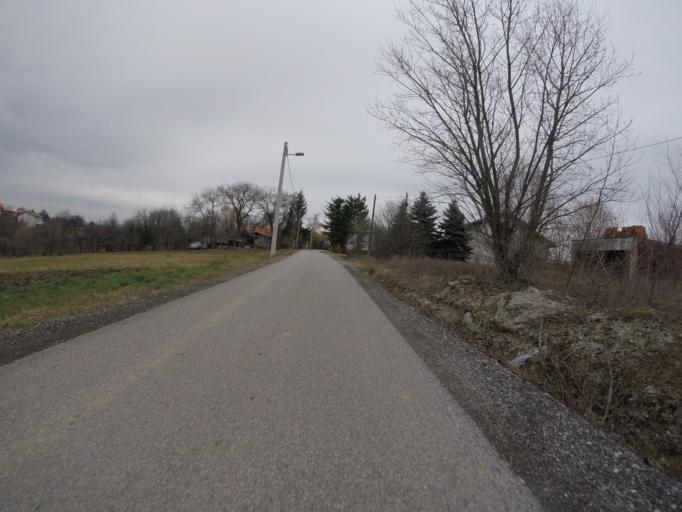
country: HR
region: Grad Zagreb
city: Strmec
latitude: 45.6630
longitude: 15.8733
